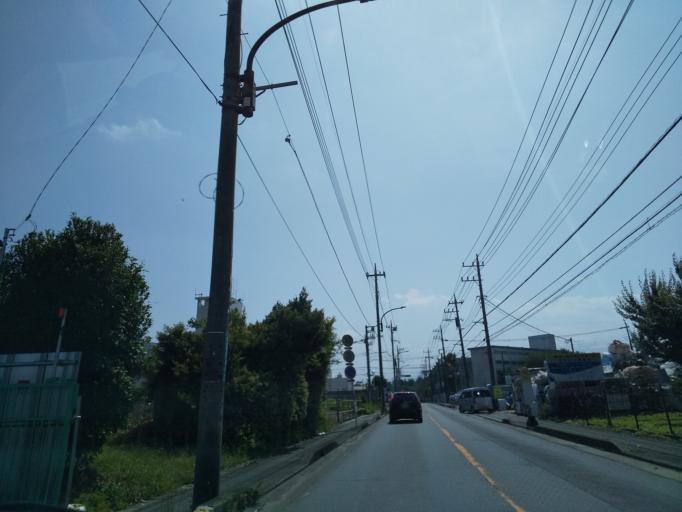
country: JP
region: Kanagawa
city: Zama
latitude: 35.5144
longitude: 139.4032
